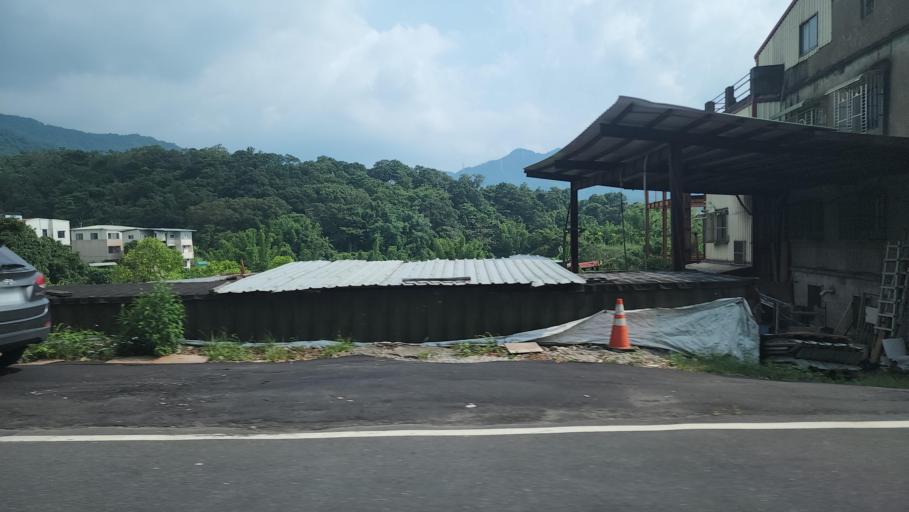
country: TW
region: Taiwan
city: Daxi
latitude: 24.9118
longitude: 121.3763
